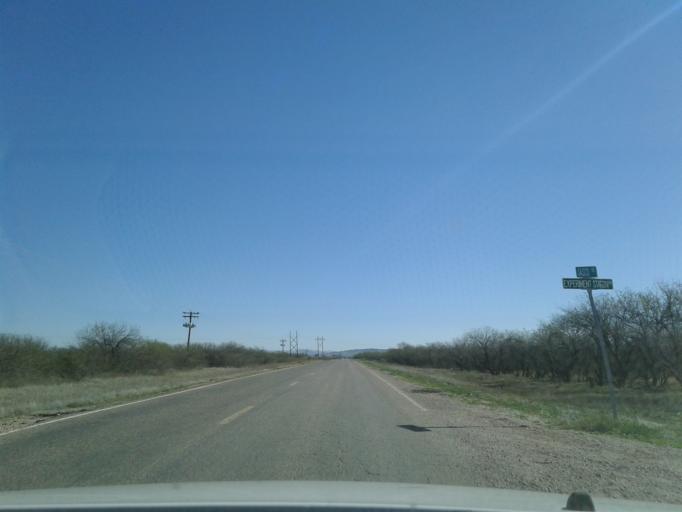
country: US
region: Arizona
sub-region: Pima County
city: Avra Valley
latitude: 32.5609
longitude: -111.3625
